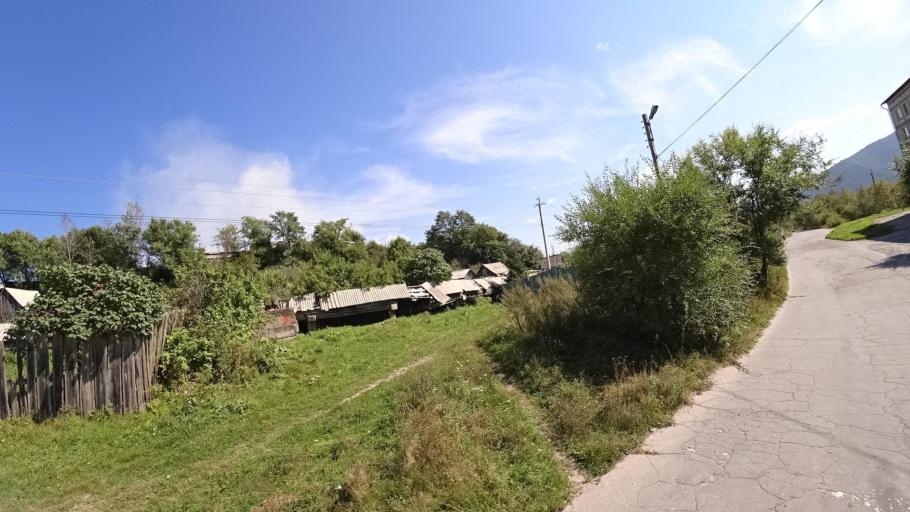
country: RU
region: Jewish Autonomous Oblast
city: Londoko
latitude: 49.0103
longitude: 131.8872
